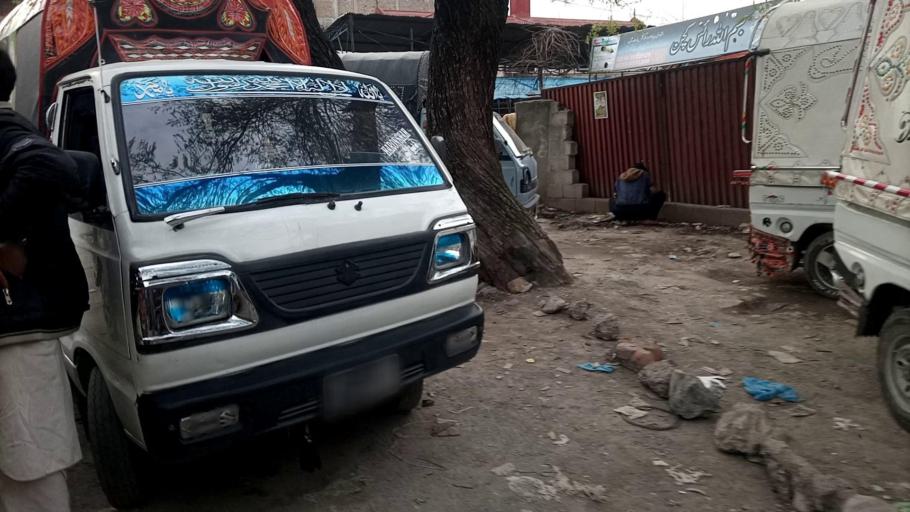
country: PK
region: Khyber Pakhtunkhwa
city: Abbottabad
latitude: 34.1454
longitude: 73.2186
